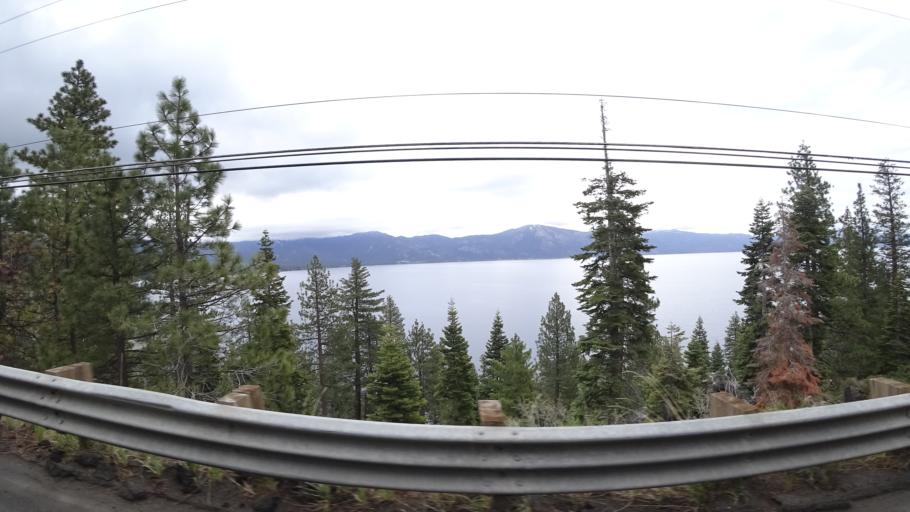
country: US
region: California
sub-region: Placer County
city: Kings Beach
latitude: 39.2350
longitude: -120.0023
